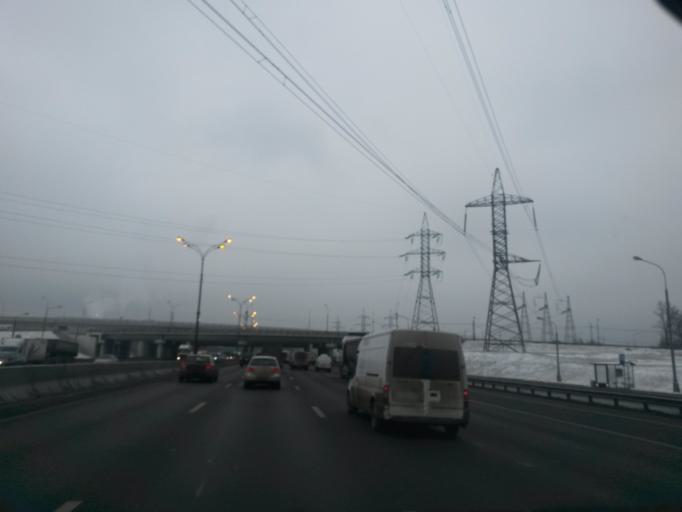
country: RU
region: Moskovskaya
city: Vostryakovo
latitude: 55.6605
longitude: 37.4344
